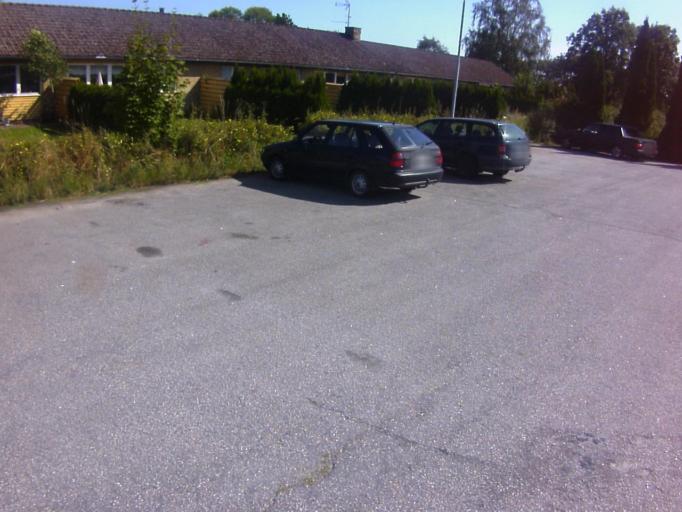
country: SE
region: Blekinge
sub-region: Solvesborgs Kommun
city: Soelvesborg
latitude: 56.1078
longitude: 14.6187
